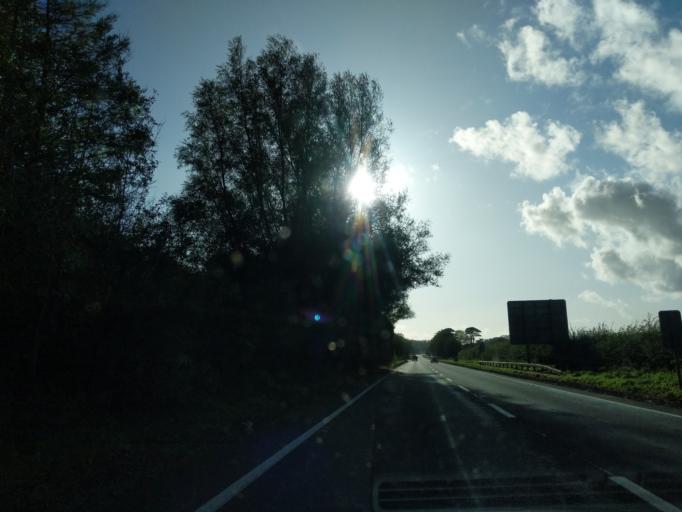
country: GB
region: Scotland
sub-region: Dumfries and Galloway
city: Castle Douglas
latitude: 54.9288
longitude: -3.9539
